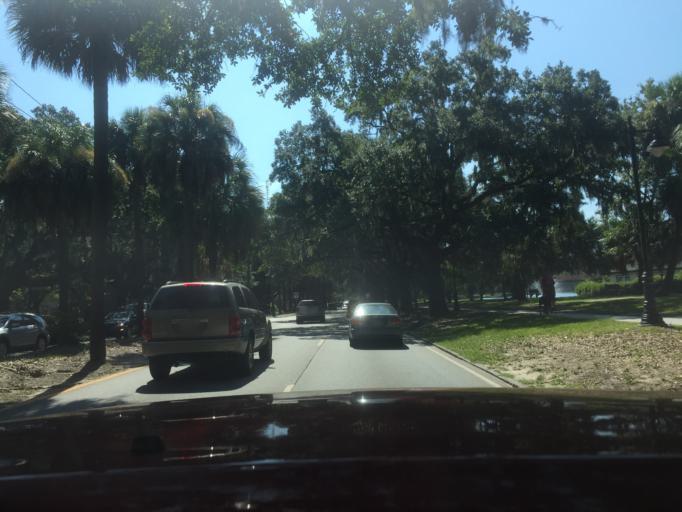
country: US
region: Georgia
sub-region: Chatham County
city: Thunderbolt
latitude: 32.0479
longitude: -81.0844
